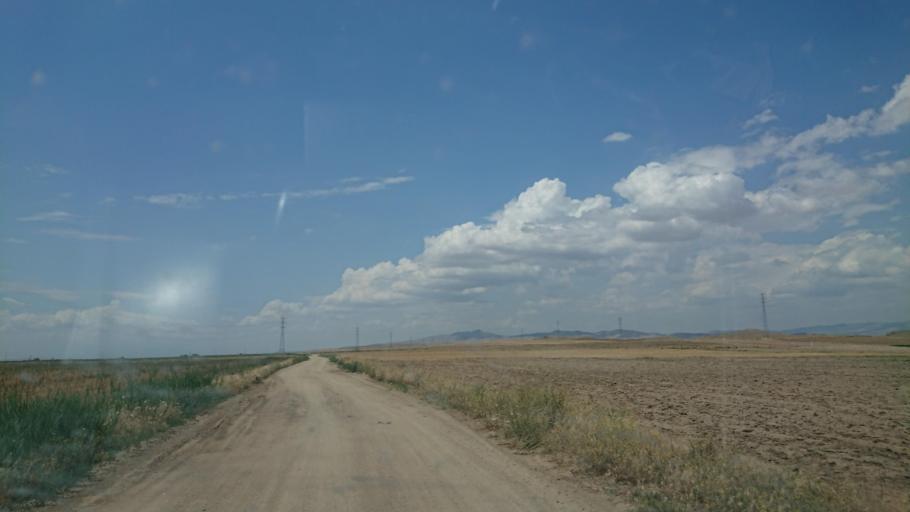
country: TR
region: Aksaray
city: Sariyahsi
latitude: 39.0078
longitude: 33.8832
